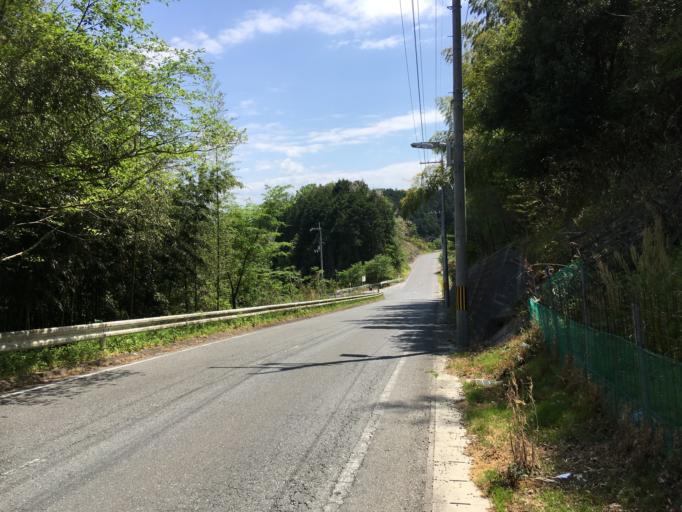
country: JP
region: Nara
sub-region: Ikoma-shi
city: Ikoma
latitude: 34.6477
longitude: 135.6847
